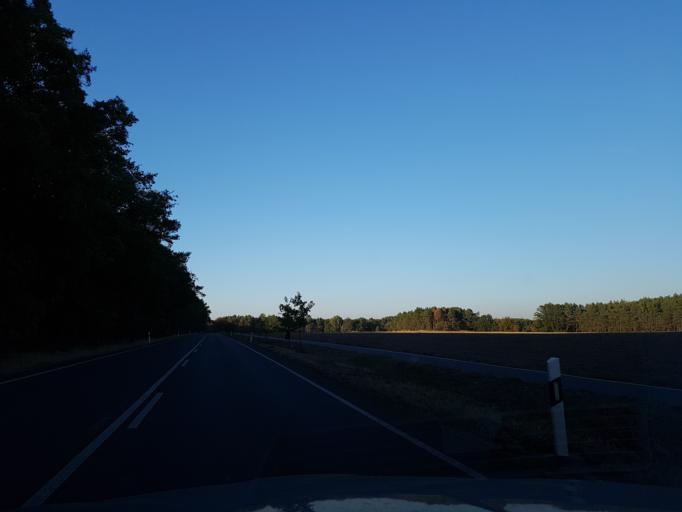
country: DE
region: Brandenburg
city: Bad Liebenwerda
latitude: 51.5352
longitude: 13.3969
